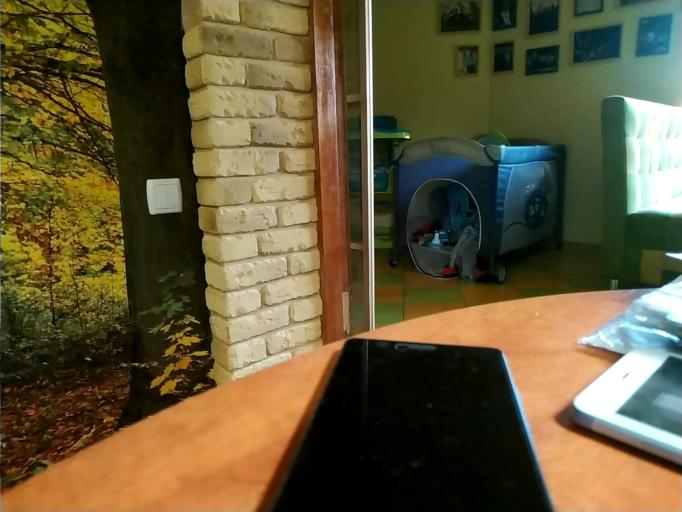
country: RU
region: Kaluga
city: Seredeyskiy
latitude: 53.7597
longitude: 35.4087
